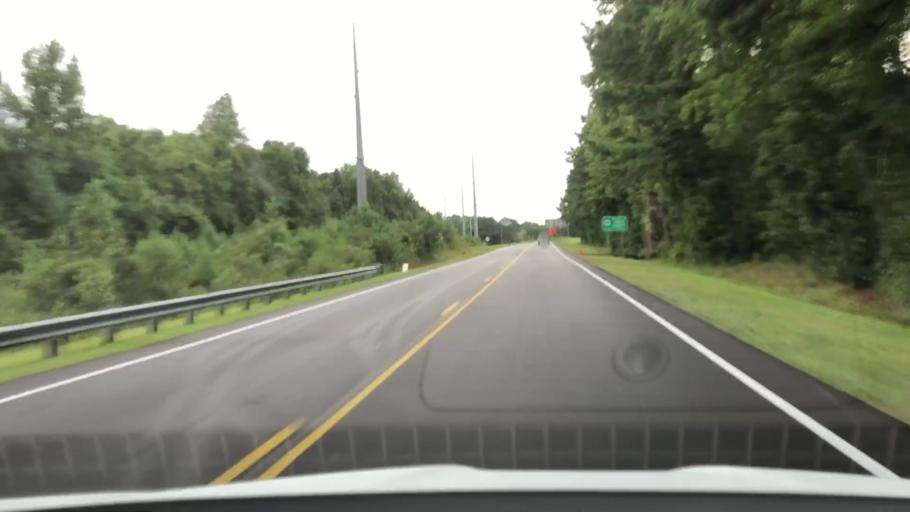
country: US
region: North Carolina
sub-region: Onslow County
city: Swansboro
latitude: 34.7992
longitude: -77.1317
